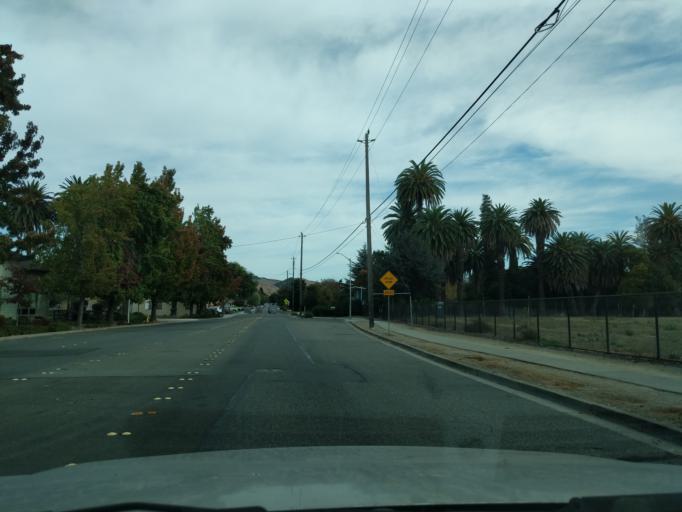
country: US
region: California
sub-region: Alameda County
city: Fremont
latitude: 37.5793
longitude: -121.9894
